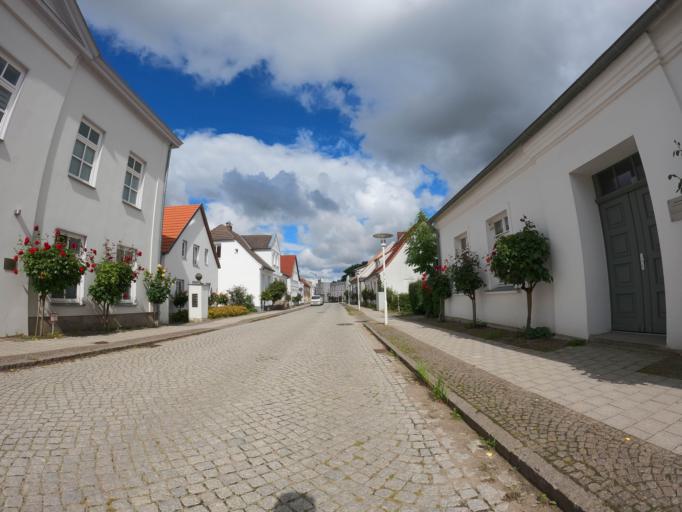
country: DE
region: Mecklenburg-Vorpommern
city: Putbus
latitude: 54.3550
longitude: 13.4698
